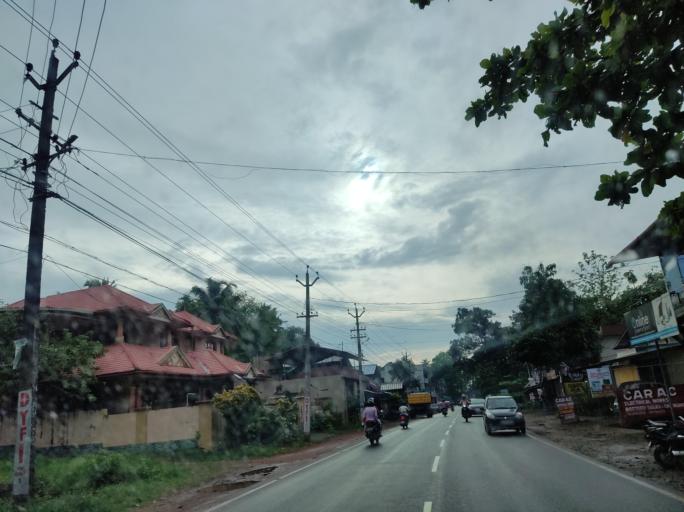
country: IN
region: Kerala
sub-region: Pattanamtitta
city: Adur
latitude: 9.1730
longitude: 76.6467
